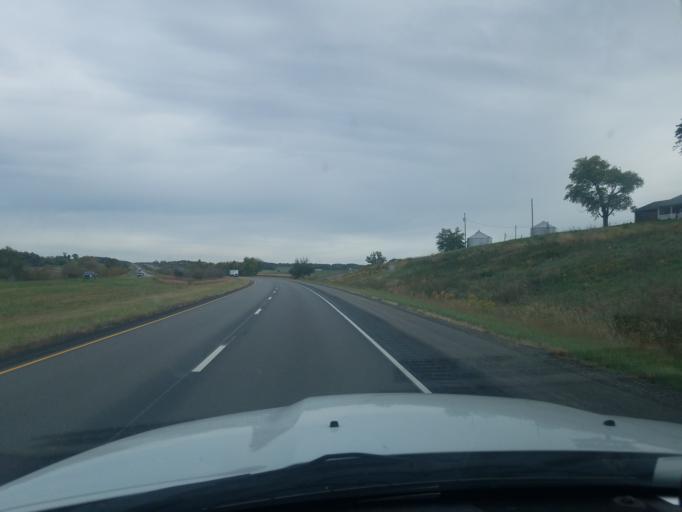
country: US
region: Indiana
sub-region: Dubois County
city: Ferdinand
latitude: 38.1993
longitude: -86.9182
